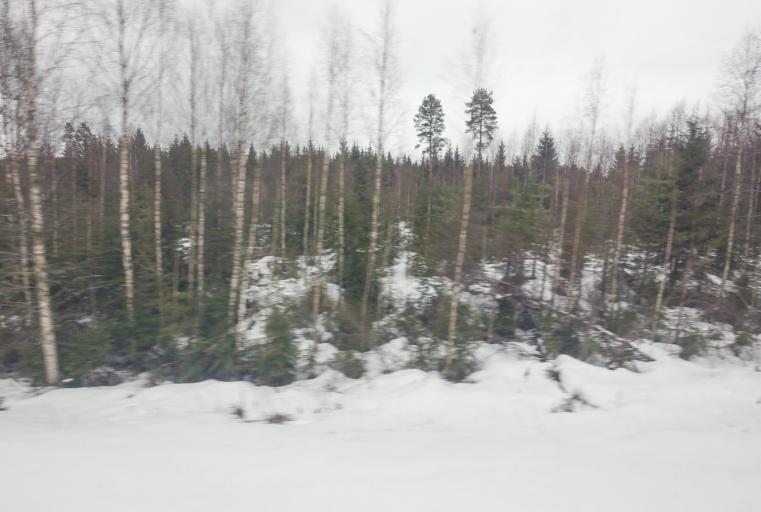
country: FI
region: Southern Savonia
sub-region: Savonlinna
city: Savonlinna
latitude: 61.8675
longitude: 29.0435
